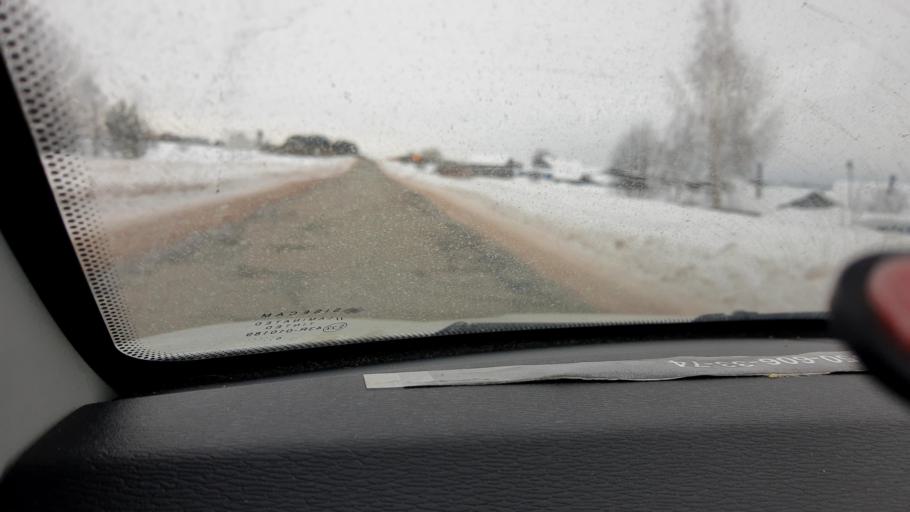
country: RU
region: Nizjnij Novgorod
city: Prudy
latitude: 57.3966
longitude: 46.0866
